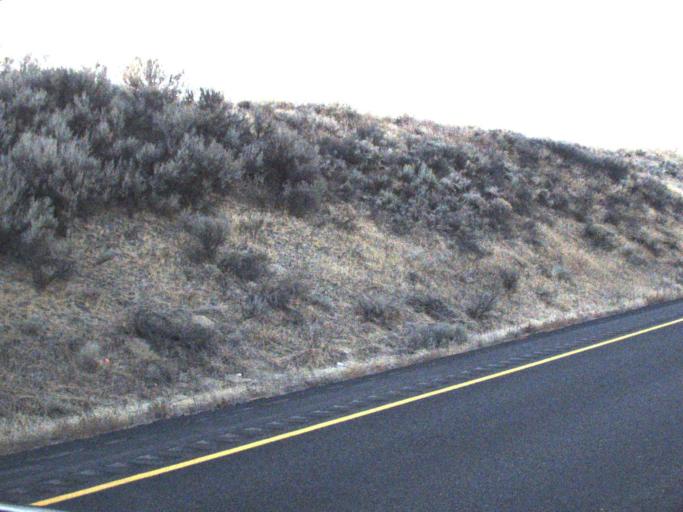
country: US
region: Washington
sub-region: Adams County
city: Ritzville
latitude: 46.9204
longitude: -118.6006
